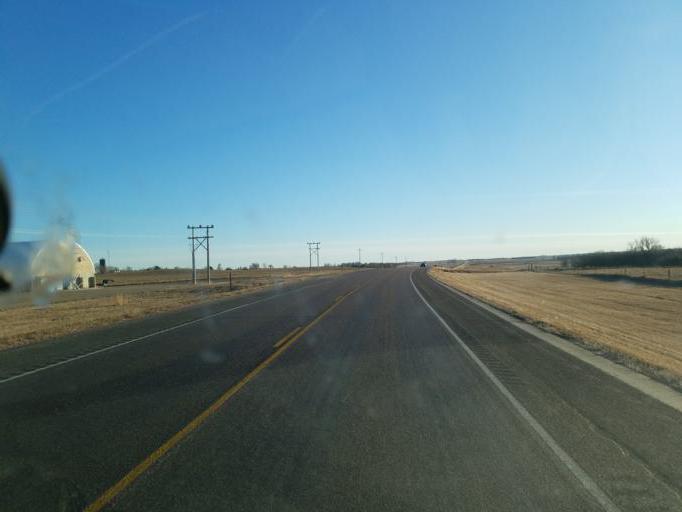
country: US
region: South Dakota
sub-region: Hutchinson County
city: Parkston
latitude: 43.2204
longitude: -97.9727
